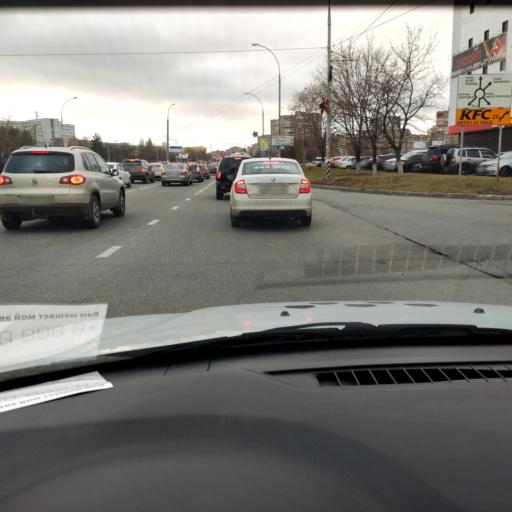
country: RU
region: Samara
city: Tol'yatti
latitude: 53.5258
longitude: 49.3287
